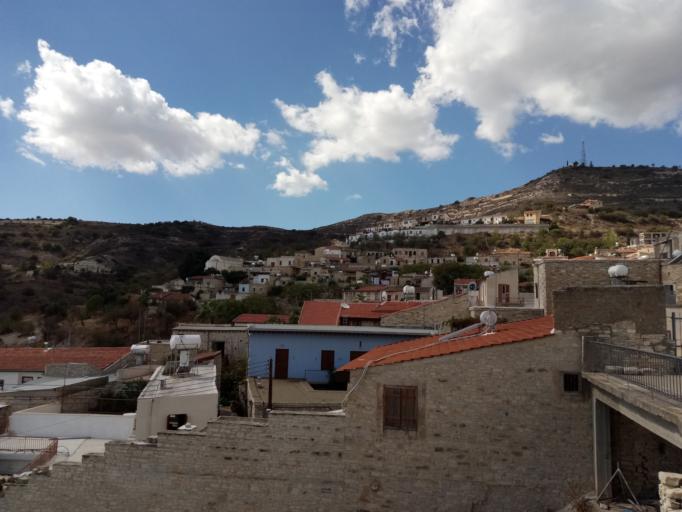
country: CY
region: Lefkosia
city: Lythrodontas
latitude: 34.8656
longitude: 33.3085
